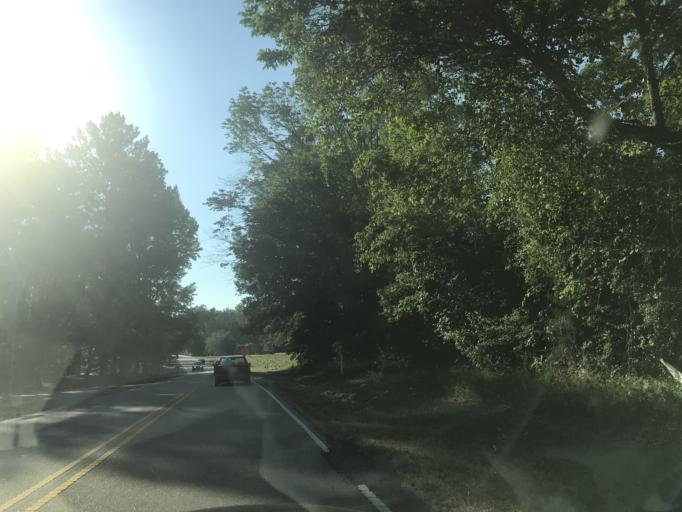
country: US
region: North Carolina
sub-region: Wake County
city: Garner
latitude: 35.7335
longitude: -78.6031
